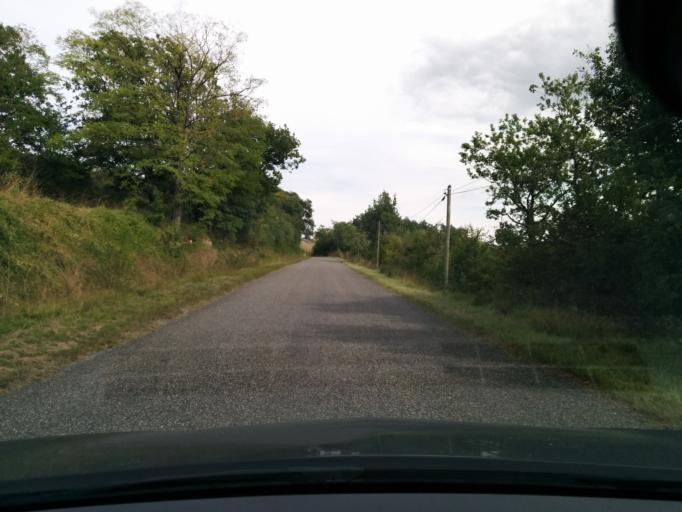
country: FR
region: Midi-Pyrenees
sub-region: Departement du Gers
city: Aubiet
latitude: 43.5718
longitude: 0.7325
